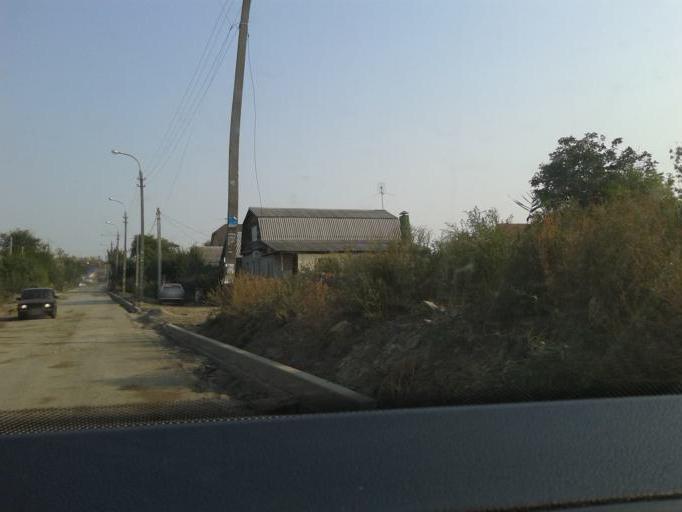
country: RU
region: Volgograd
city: Volgograd
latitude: 48.6137
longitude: 44.4140
